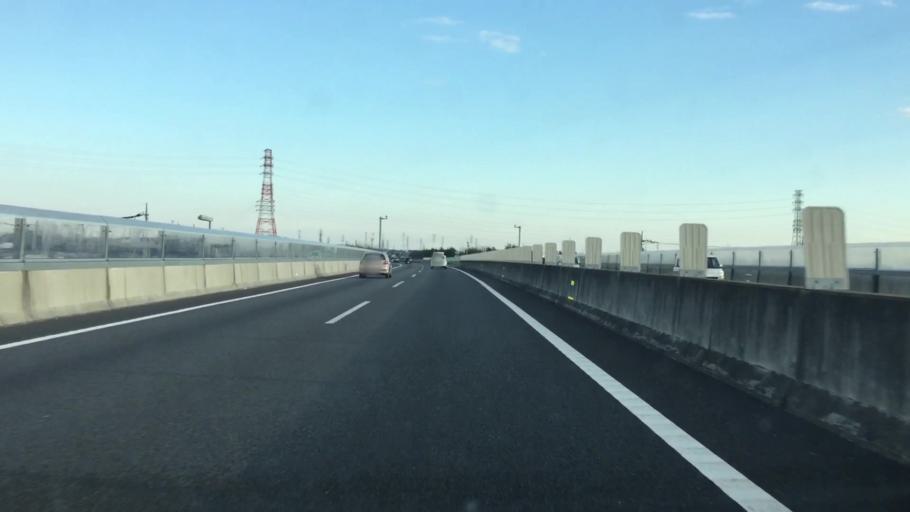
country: JP
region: Gunma
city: Isesaki
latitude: 36.3459
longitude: 139.2488
